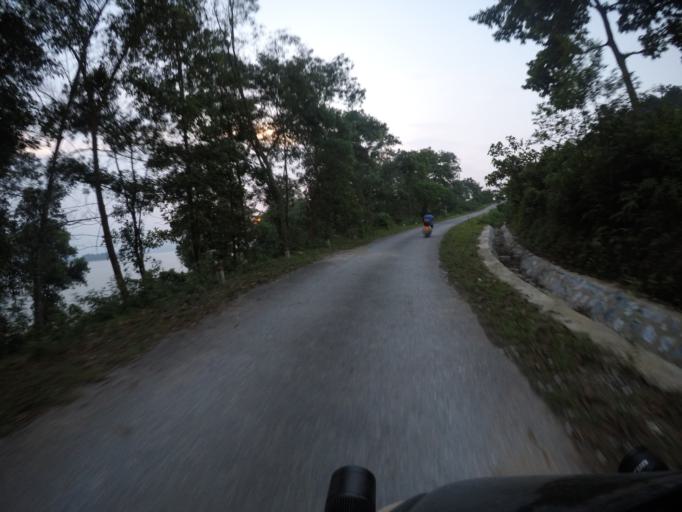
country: VN
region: Thai Nguyen
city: Chua Hang
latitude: 21.5845
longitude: 105.7011
